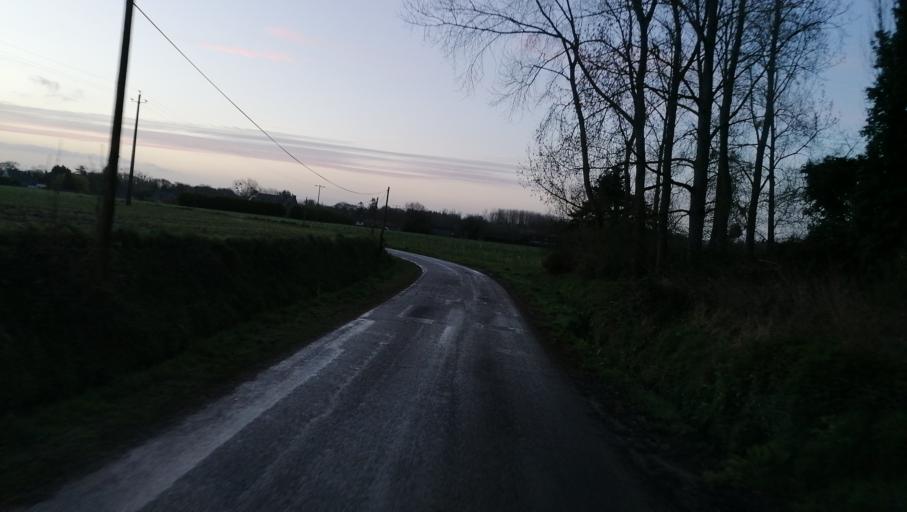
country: FR
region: Brittany
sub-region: Departement des Cotes-d'Armor
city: Plouha
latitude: 48.6677
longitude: -2.9528
